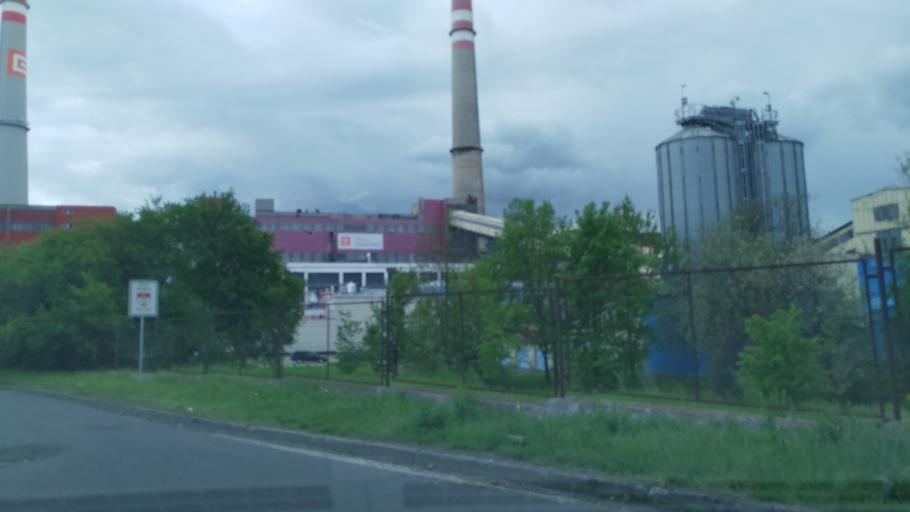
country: CZ
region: Ustecky
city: Trmice
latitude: 50.6470
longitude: 13.9882
